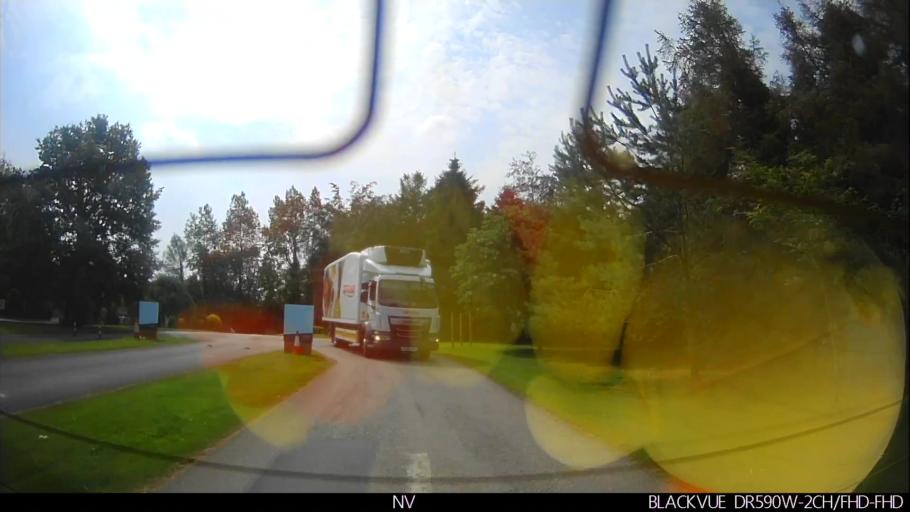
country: GB
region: England
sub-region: North Yorkshire
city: Great Habton
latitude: 54.2060
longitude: -0.8095
